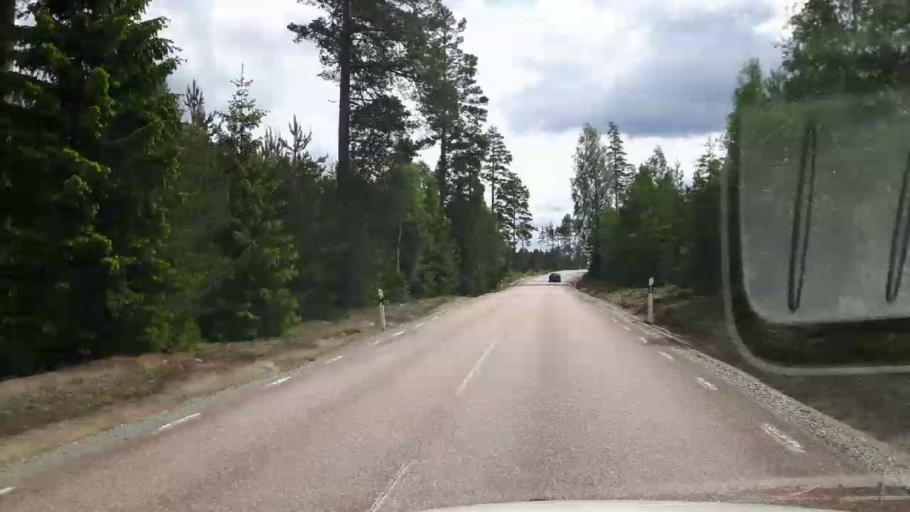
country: SE
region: Vaestmanland
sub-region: Skinnskattebergs Kommun
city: Skinnskatteberg
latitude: 59.8260
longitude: 15.8347
